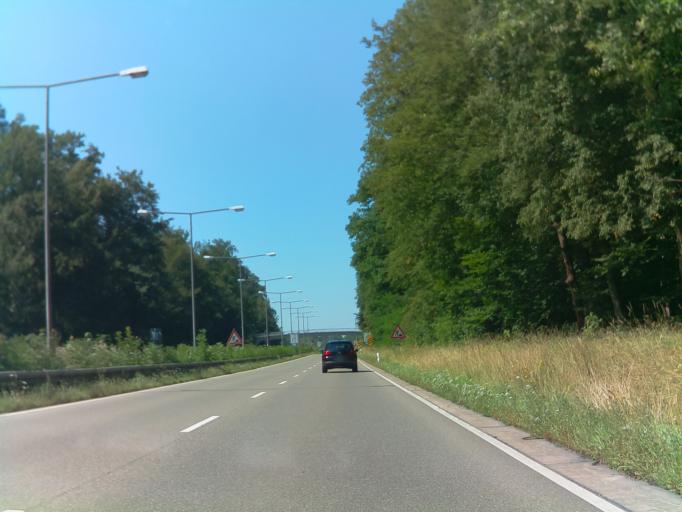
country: DE
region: Baden-Wuerttemberg
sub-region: Regierungsbezirk Stuttgart
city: Gerlingen
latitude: 48.7742
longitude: 9.0984
